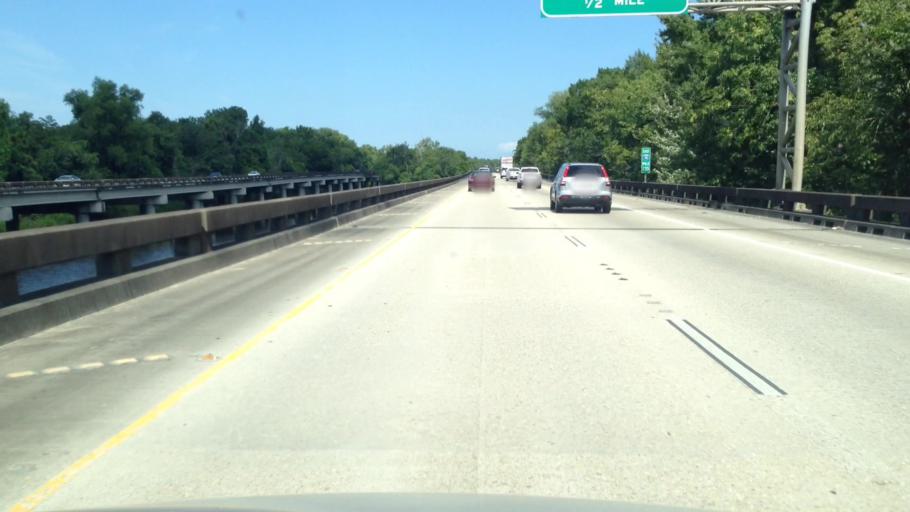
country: US
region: Louisiana
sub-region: Saint John the Baptist Parish
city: Montegut
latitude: 30.1080
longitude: -90.5126
